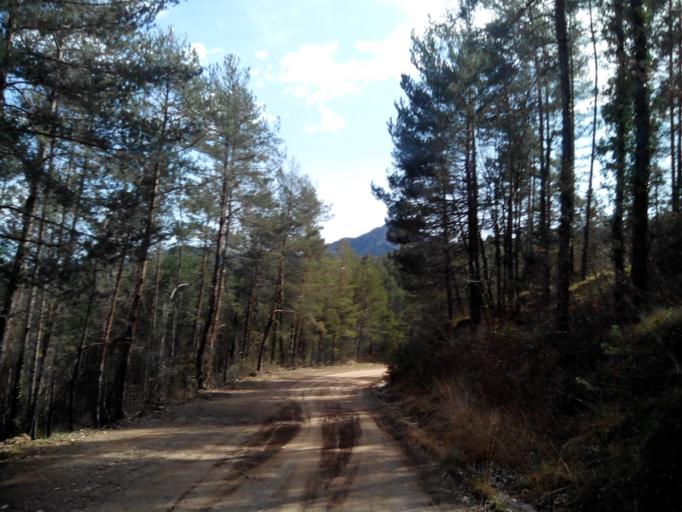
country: ES
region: Catalonia
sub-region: Provincia de Barcelona
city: Vilada
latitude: 42.1424
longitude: 1.9299
